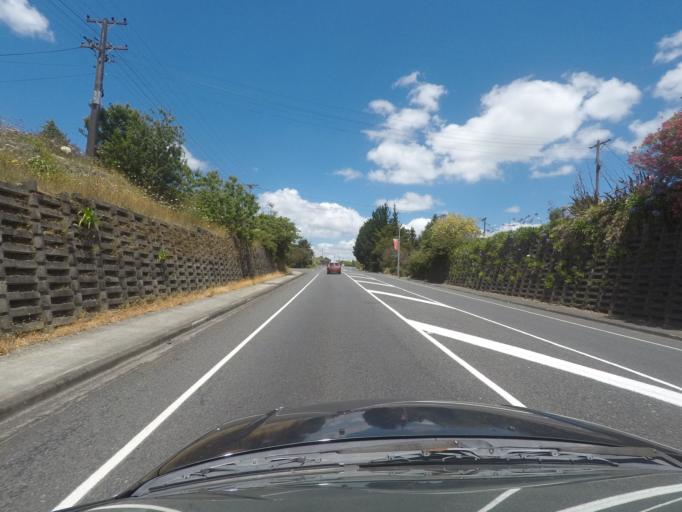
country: NZ
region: Northland
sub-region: Whangarei
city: Whangarei
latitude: -35.7450
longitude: 174.3666
